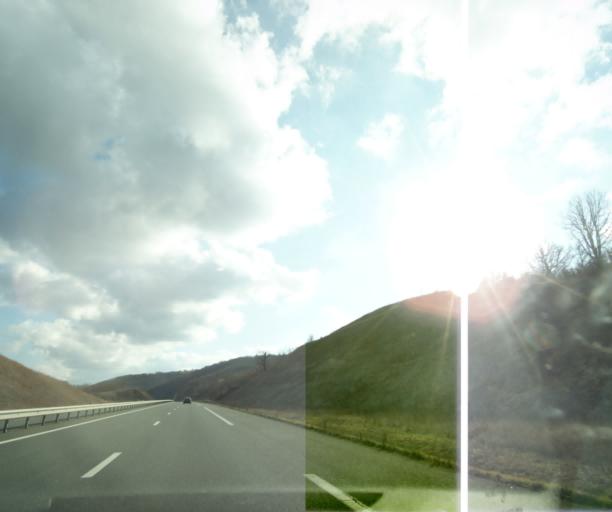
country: FR
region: Midi-Pyrenees
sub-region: Departement du Lot
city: Le Vigan
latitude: 44.8088
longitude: 1.5040
